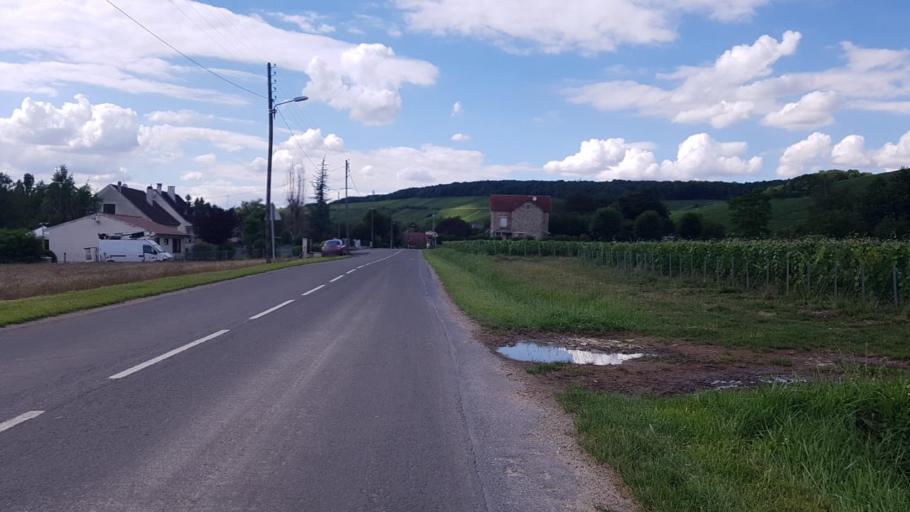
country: FR
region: Picardie
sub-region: Departement de l'Aisne
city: Crezancy
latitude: 49.0767
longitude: 3.5613
